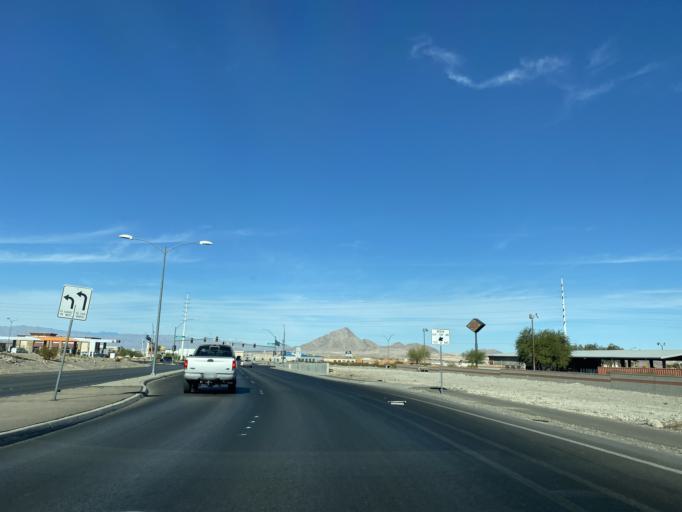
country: US
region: Nevada
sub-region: Clark County
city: Henderson
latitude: 36.0623
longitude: -115.0271
